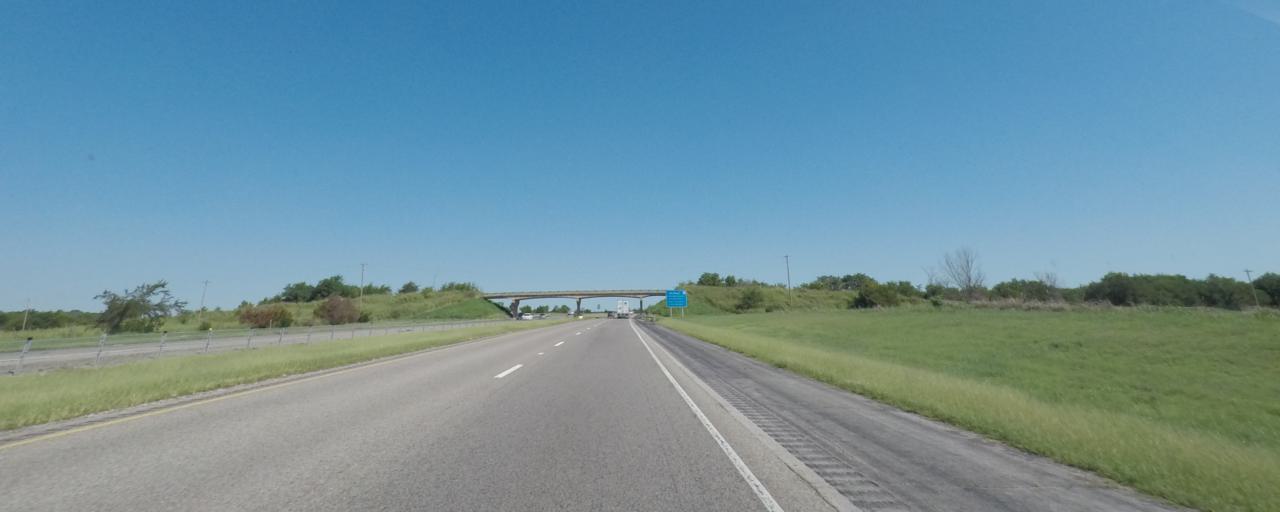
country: US
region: Oklahoma
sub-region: Noble County
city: Perry
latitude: 36.2588
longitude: -97.3261
